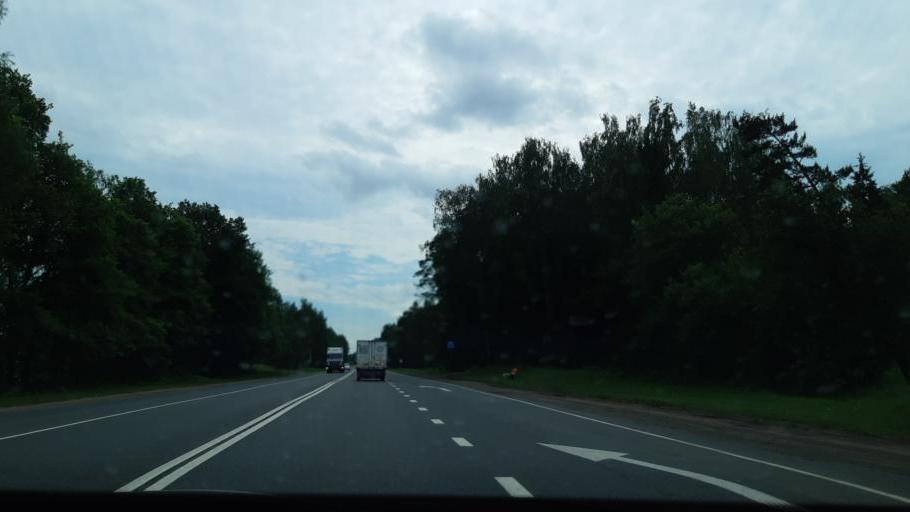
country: RU
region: Moskovskaya
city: Dorokhovo
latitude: 55.4606
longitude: 36.3540
